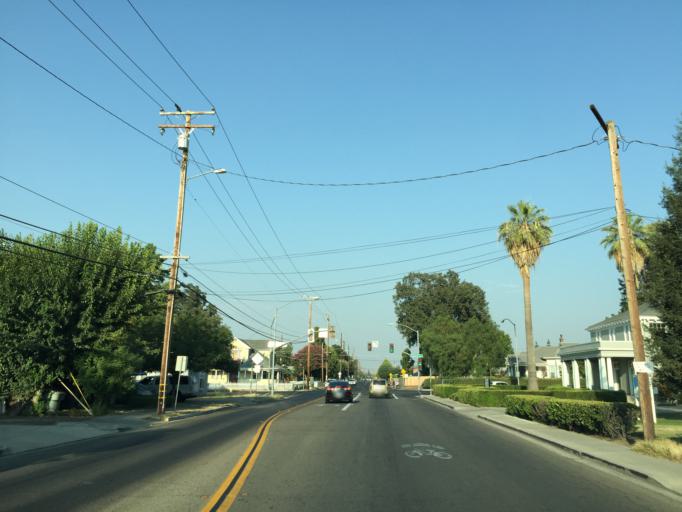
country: US
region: California
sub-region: Tulare County
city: Visalia
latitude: 36.3201
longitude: -119.2931
